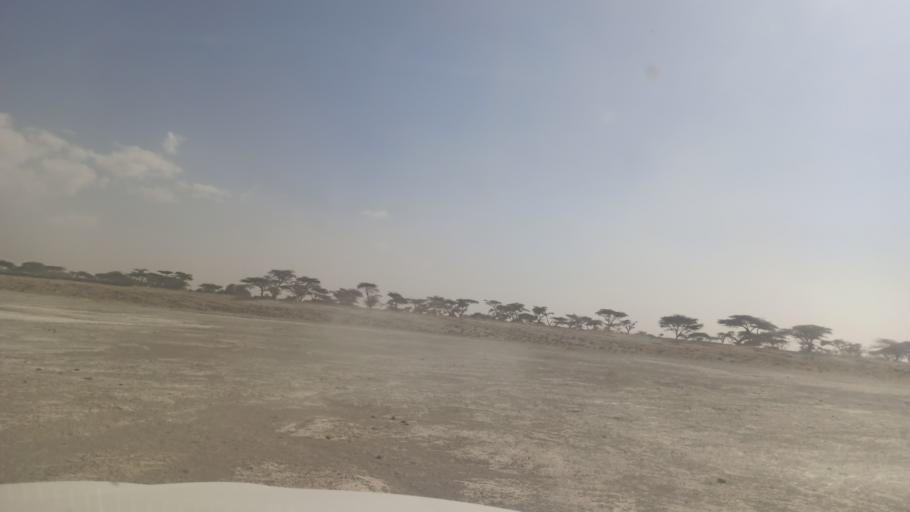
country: ET
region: Oromiya
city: Ziway
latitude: 7.6884
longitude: 38.6541
